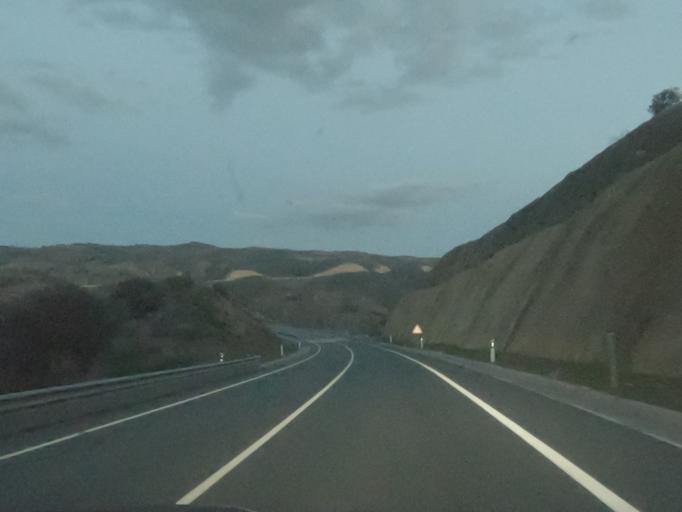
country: PT
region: Braganca
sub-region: Alfandega da Fe
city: Alfandega da Fe
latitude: 41.3084
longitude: -6.9232
